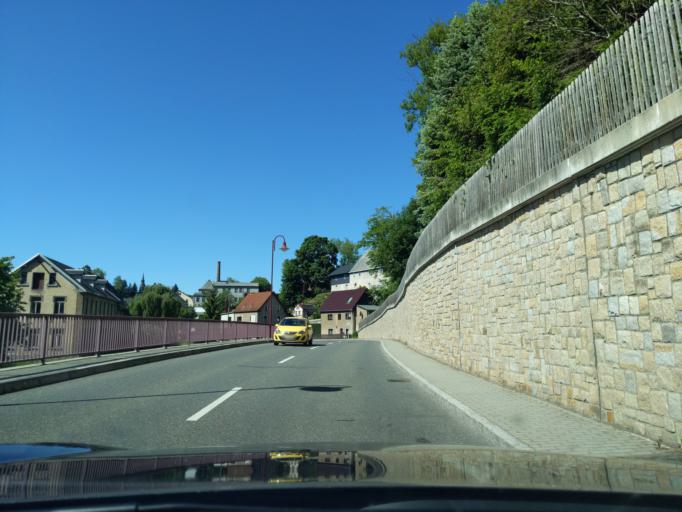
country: DE
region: Saxony
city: Stutzengrun
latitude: 50.5704
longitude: 12.5355
